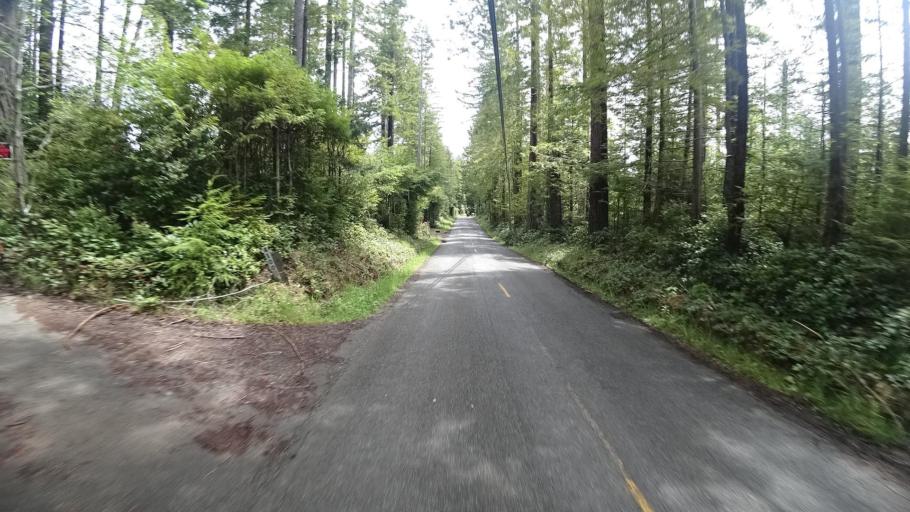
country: US
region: California
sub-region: Humboldt County
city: Bayside
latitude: 40.7952
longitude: -124.0292
